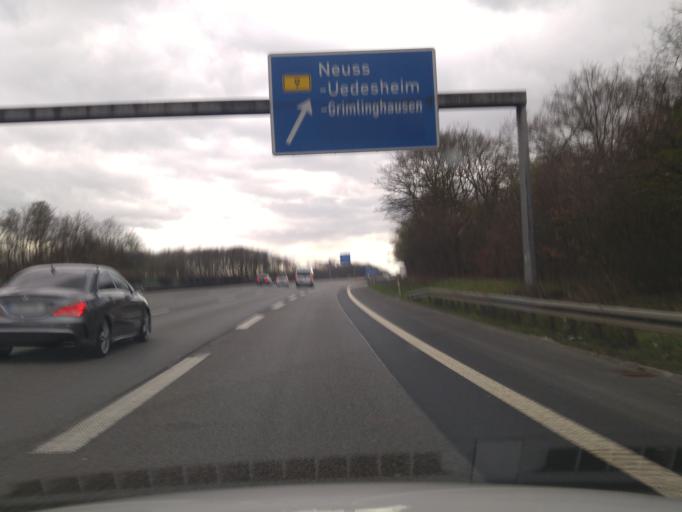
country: DE
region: North Rhine-Westphalia
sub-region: Regierungsbezirk Dusseldorf
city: Dusseldorf
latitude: 51.1659
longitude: 6.7717
